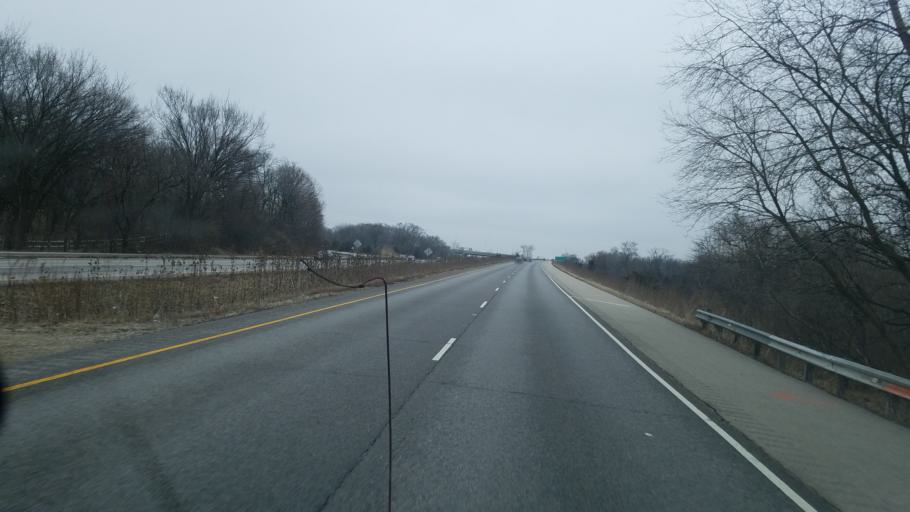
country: US
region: Illinois
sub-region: Lake County
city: Wadsworth
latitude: 42.4728
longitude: -87.9470
